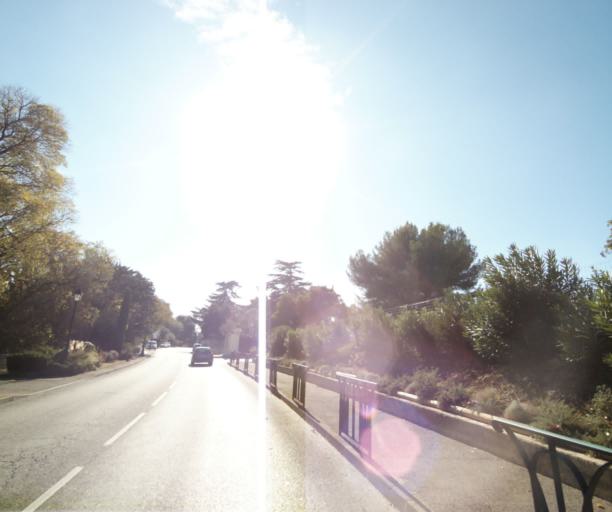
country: FR
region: Provence-Alpes-Cote d'Azur
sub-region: Departement des Bouches-du-Rhone
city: Ceyreste
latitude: 43.2112
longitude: 5.6288
